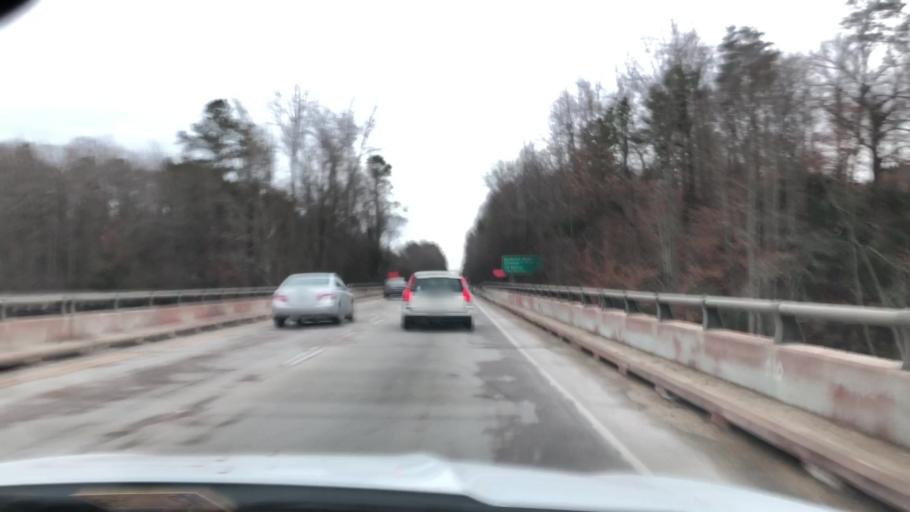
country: US
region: Virginia
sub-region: City of Williamsburg
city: Williamsburg
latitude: 37.2923
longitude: -76.6753
